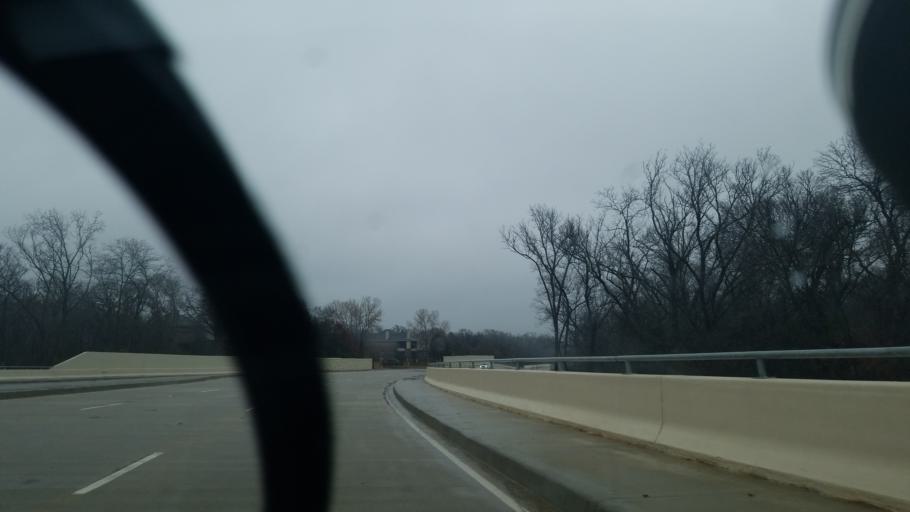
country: US
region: Texas
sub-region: Denton County
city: Corinth
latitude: 33.1361
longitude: -97.0950
